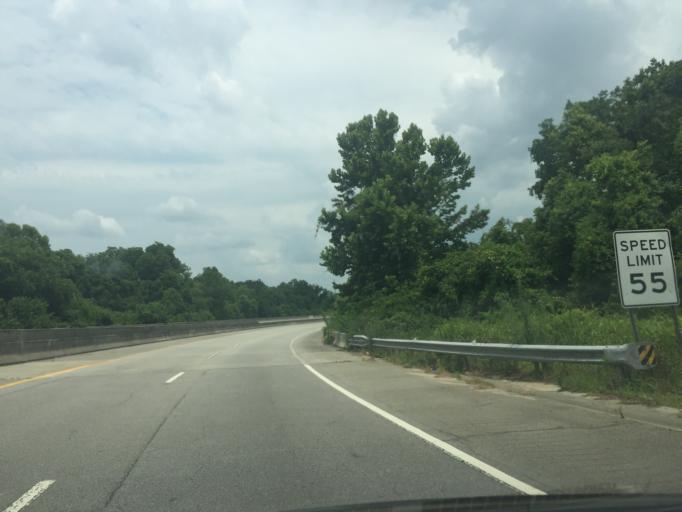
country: US
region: Georgia
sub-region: Chatham County
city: Savannah
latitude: 32.0642
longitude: -81.0747
